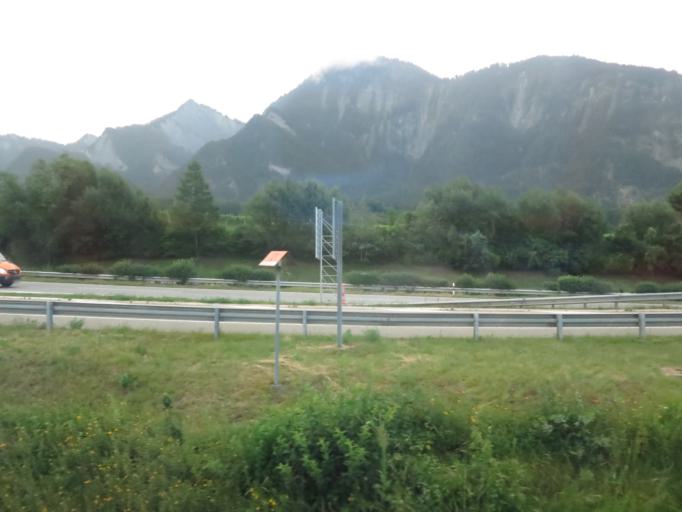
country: CH
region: Grisons
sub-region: Landquart District
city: Zizers
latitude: 46.9203
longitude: 9.5615
